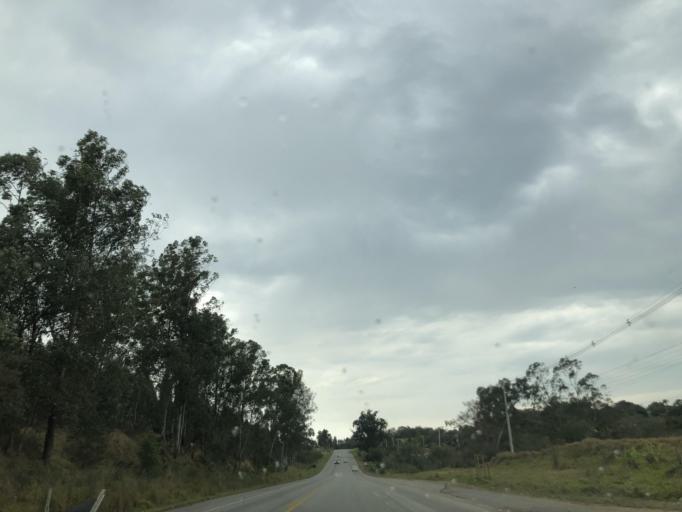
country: BR
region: Sao Paulo
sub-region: Salto De Pirapora
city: Salto de Pirapora
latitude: -23.6977
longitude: -47.6158
